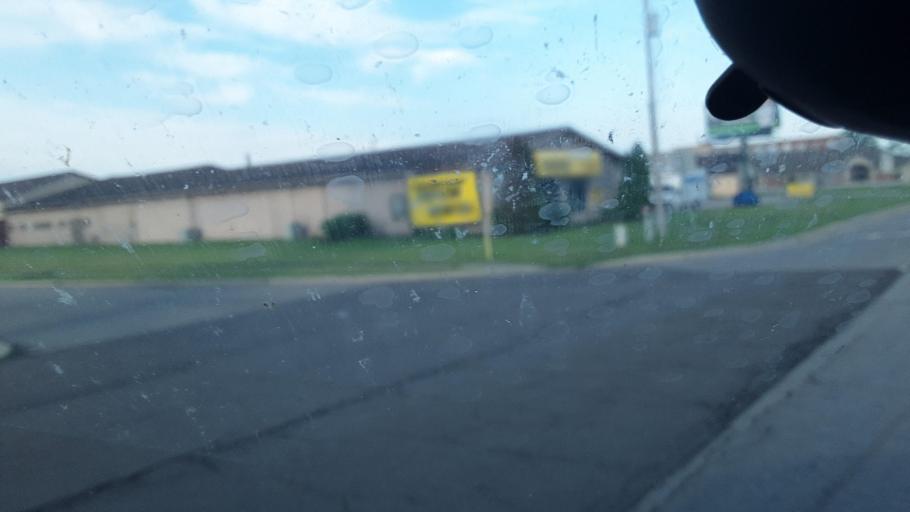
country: US
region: Indiana
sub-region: DeKalb County
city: Auburn
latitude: 41.3667
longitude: -85.0857
